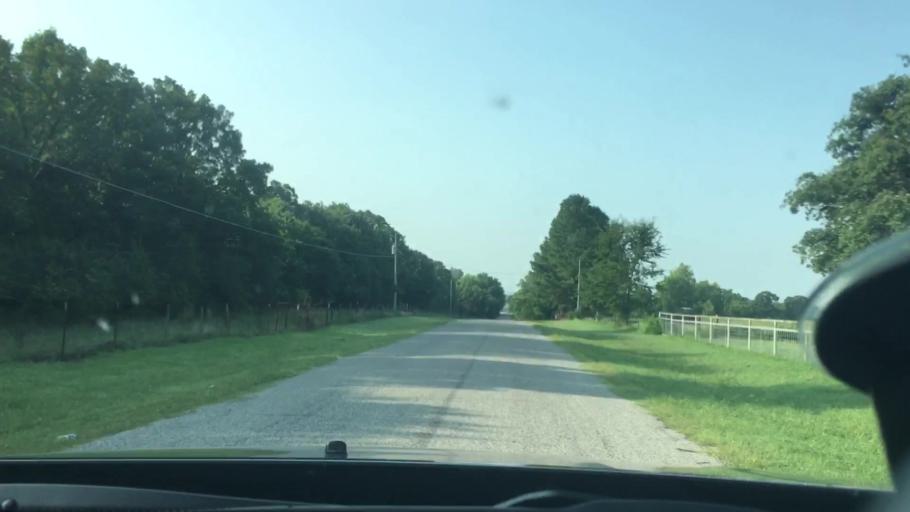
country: US
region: Oklahoma
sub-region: Pontotoc County
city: Ada
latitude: 34.7943
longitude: -96.7397
